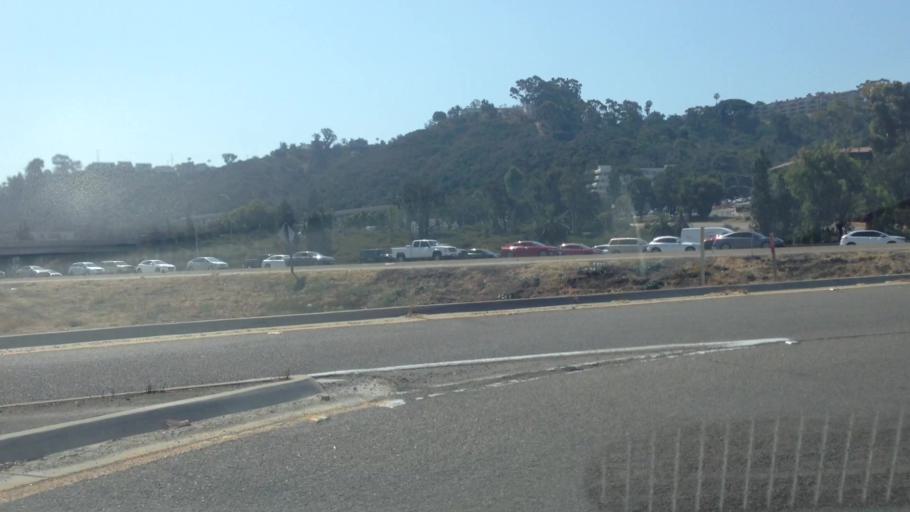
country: US
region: California
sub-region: San Diego County
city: San Diego
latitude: 32.7701
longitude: -117.1421
